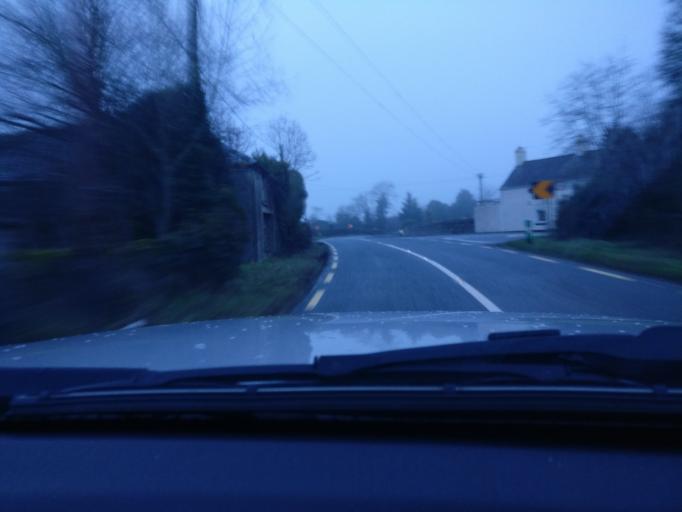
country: IE
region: Leinster
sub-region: An Mhi
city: Athboy
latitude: 53.6050
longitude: -6.9816
